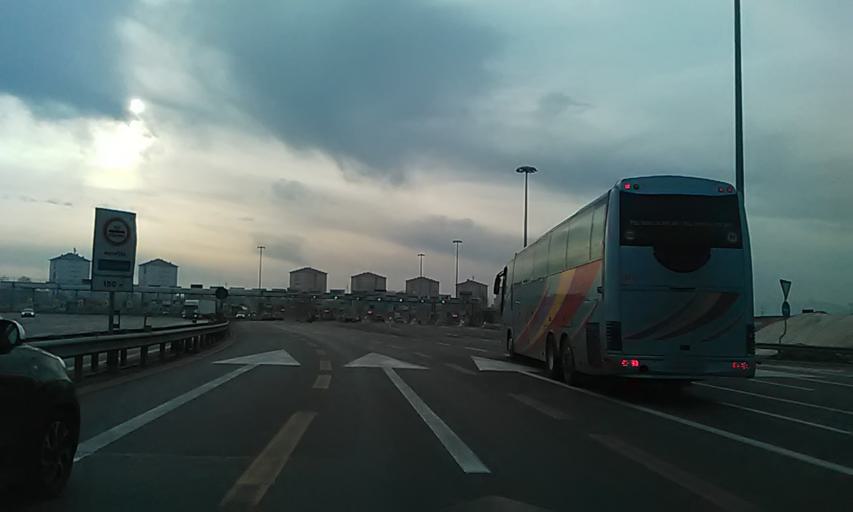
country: IT
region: Piedmont
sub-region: Provincia di Torino
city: Settimo Torinese
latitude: 45.1358
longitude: 7.7177
